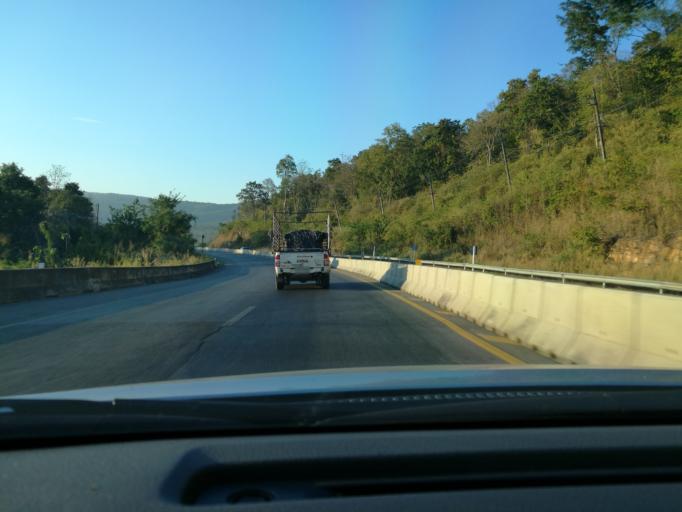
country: TH
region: Phitsanulok
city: Wang Thong
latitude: 16.8569
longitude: 100.5063
